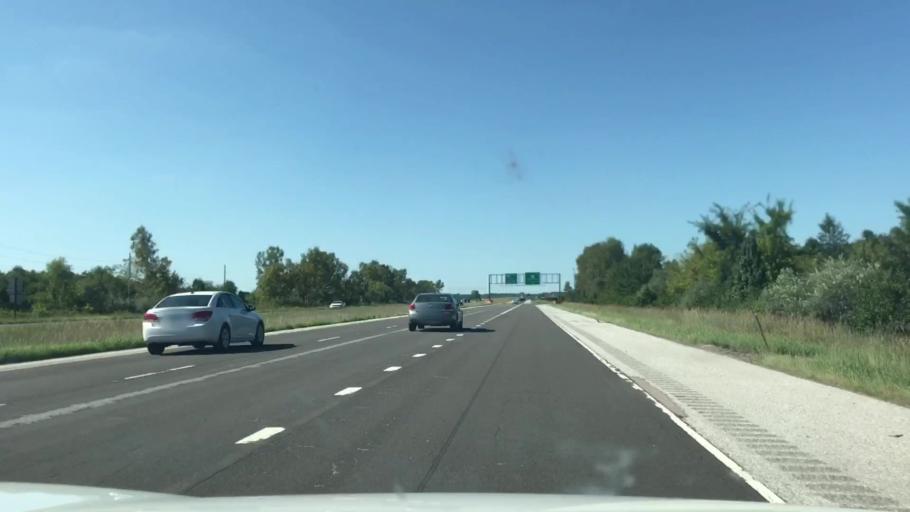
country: US
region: Illinois
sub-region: Madison County
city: South Roxana
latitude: 38.8445
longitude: -90.0468
